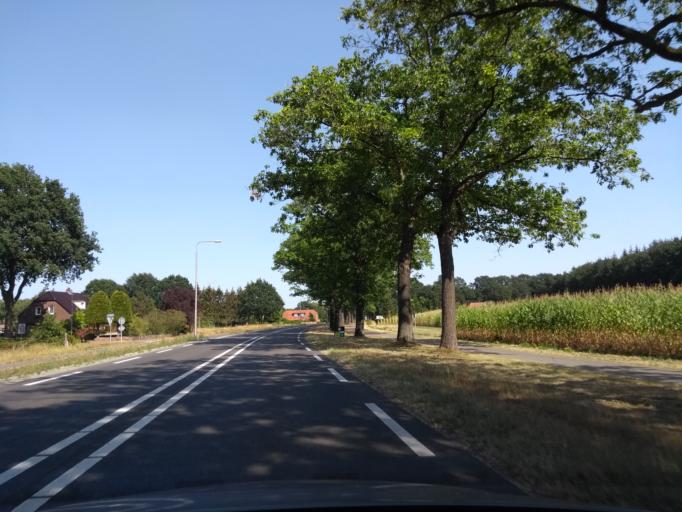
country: NL
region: Overijssel
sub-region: Gemeente Twenterand
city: Magele
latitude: 52.4649
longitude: 6.5391
